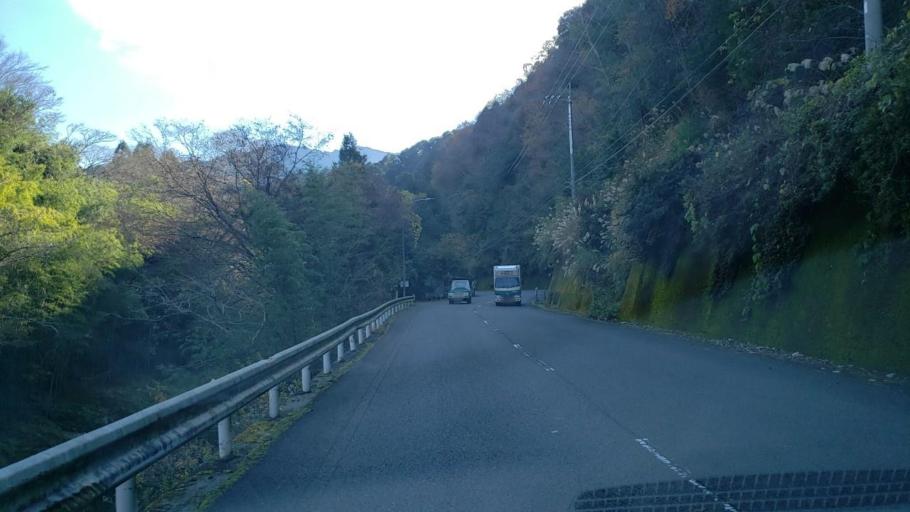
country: JP
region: Tokushima
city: Wakimachi
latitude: 34.0047
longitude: 134.0348
